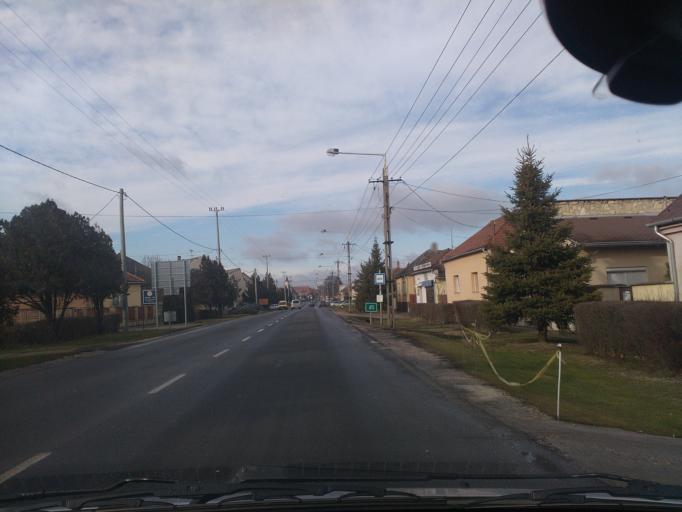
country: HU
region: Komarom-Esztergom
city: Tat
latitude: 47.7409
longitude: 18.6512
